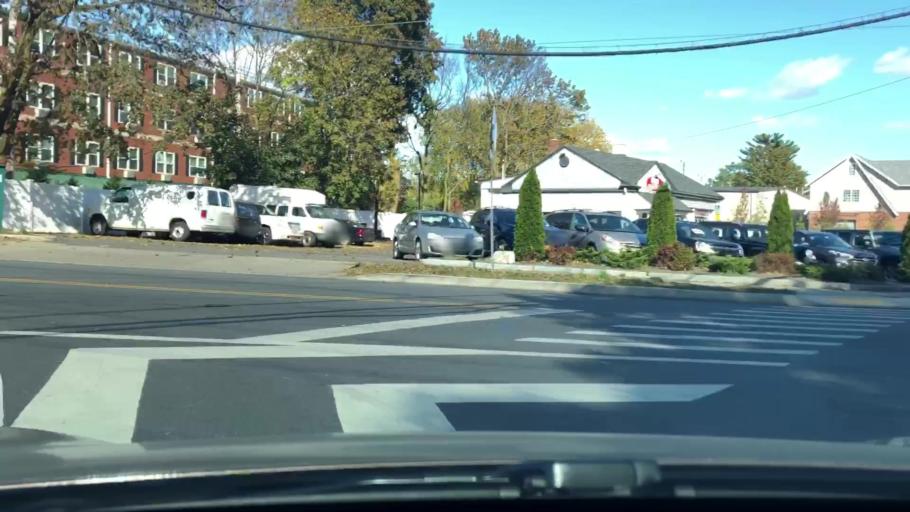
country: US
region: New York
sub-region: Westchester County
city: Rye
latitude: 40.9774
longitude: -73.6954
